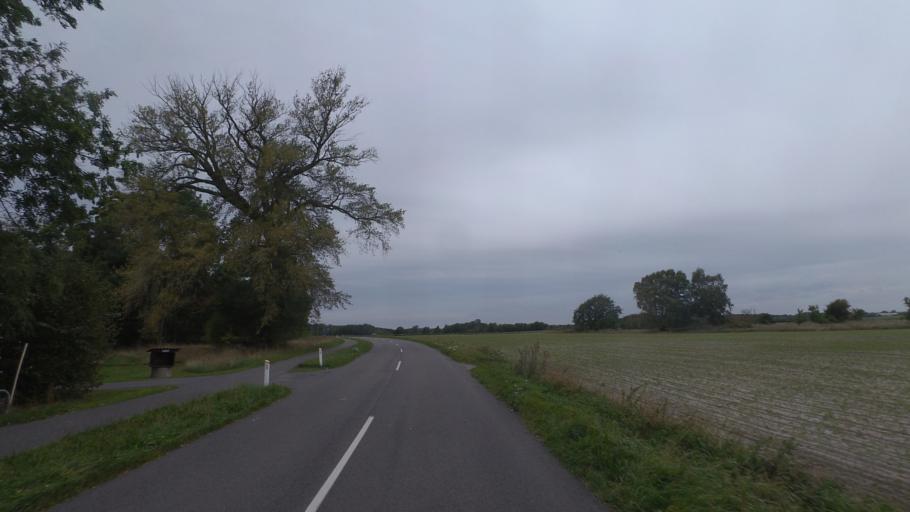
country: DK
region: Capital Region
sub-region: Bornholm Kommune
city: Nexo
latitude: 55.0034
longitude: 15.0403
